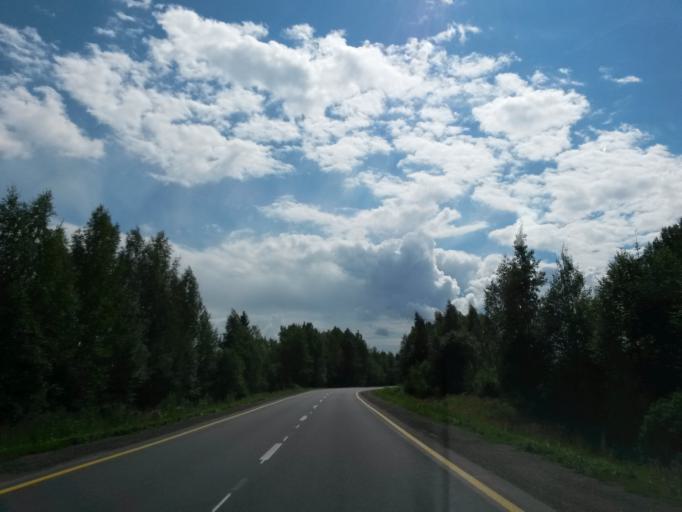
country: RU
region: Jaroslavl
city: Gavrilov-Yam
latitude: 57.2889
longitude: 39.9521
